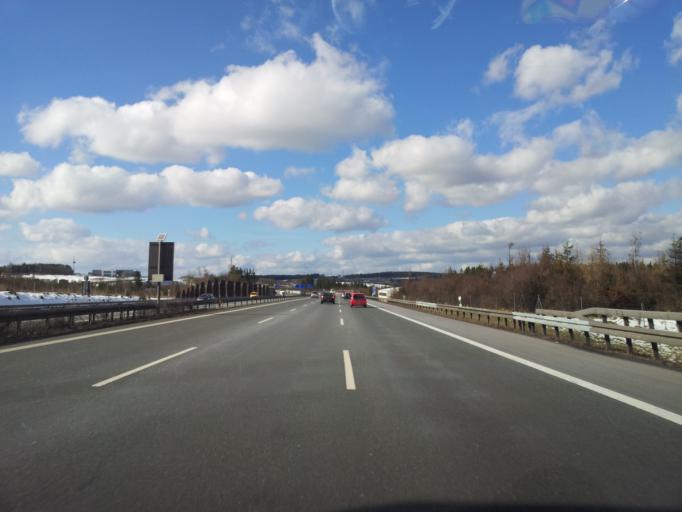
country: DE
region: Bavaria
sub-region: Upper Franconia
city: Leupoldsgrun
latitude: 50.3135
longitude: 11.8002
